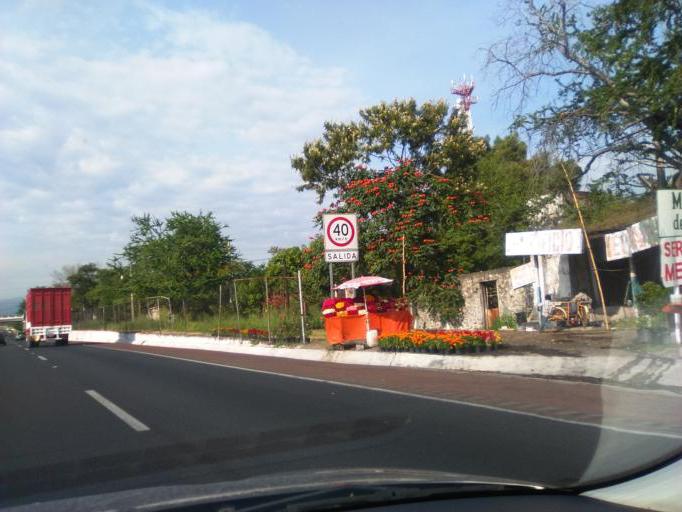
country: MX
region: Morelos
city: Temixco
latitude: 18.8577
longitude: -99.2207
